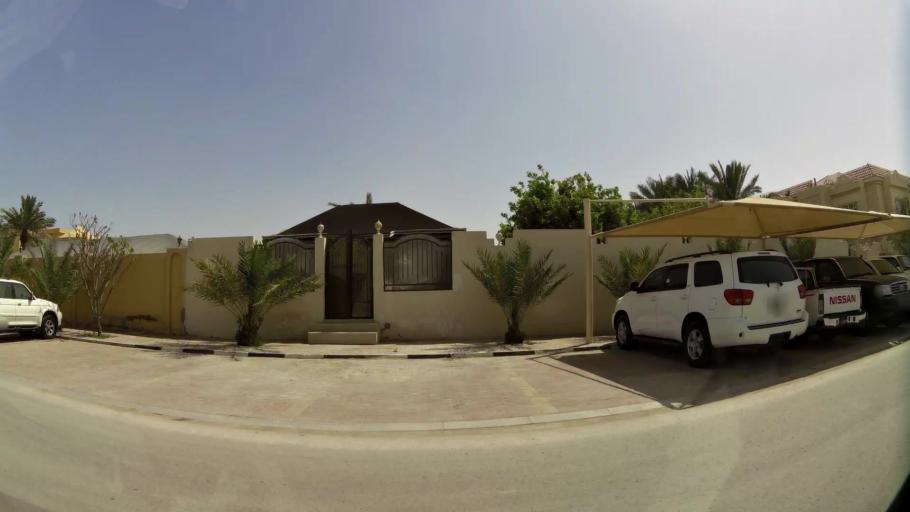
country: QA
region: Baladiyat Umm Salal
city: Umm Salal Muhammad
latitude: 25.3788
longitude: 51.4167
